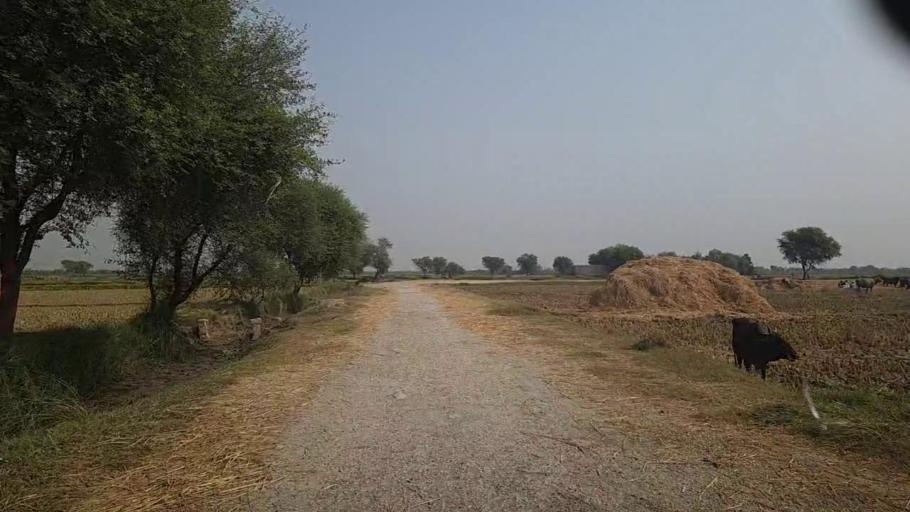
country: PK
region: Sindh
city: Kashmor
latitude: 28.3809
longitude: 69.4422
